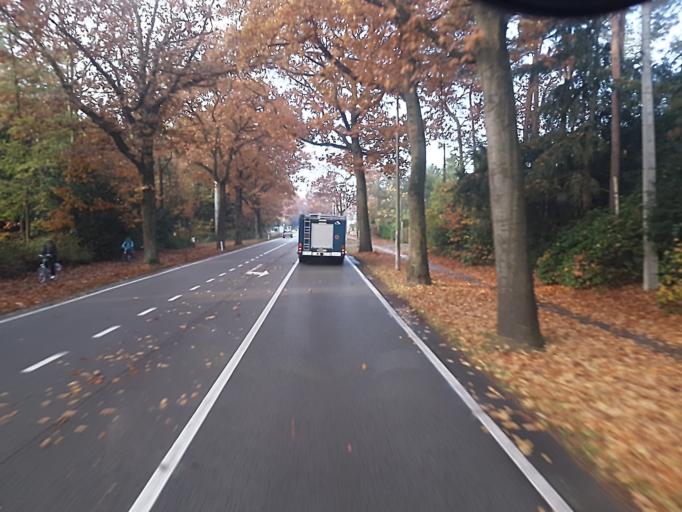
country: BE
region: Flanders
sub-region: Provincie Antwerpen
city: Vosselaar
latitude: 51.3135
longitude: 4.8781
